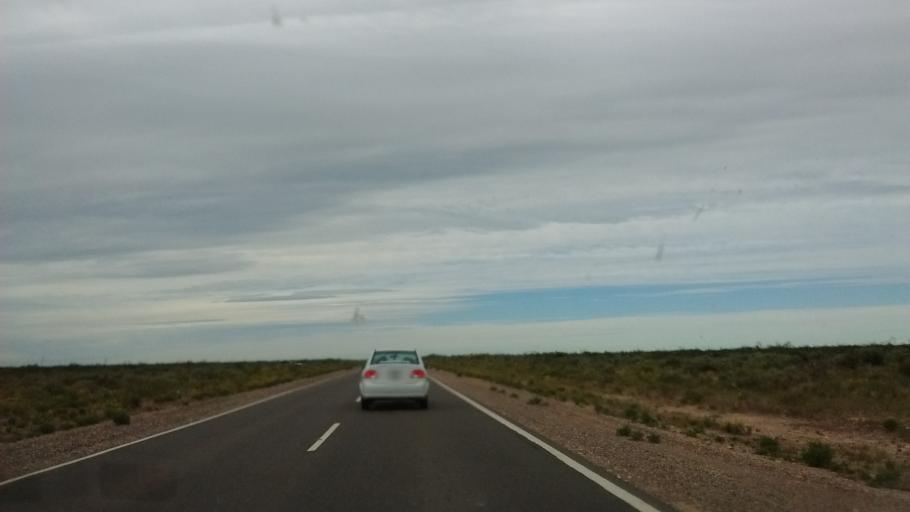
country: AR
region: Rio Negro
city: Contraalmirante Cordero
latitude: -38.3433
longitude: -68.0121
